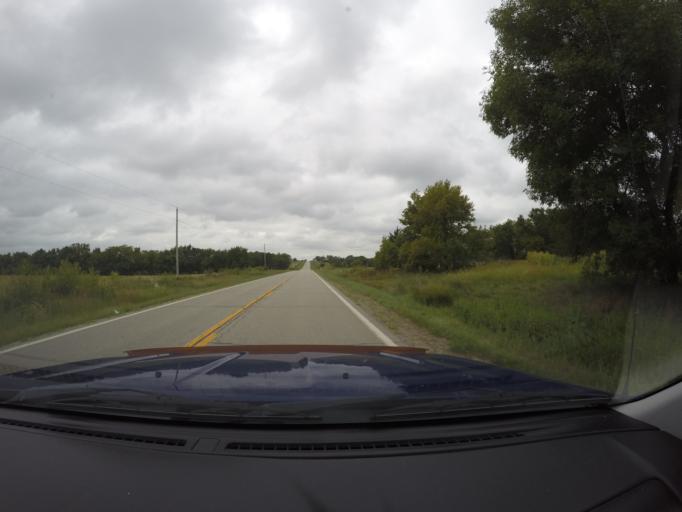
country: US
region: Kansas
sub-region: Morris County
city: Council Grove
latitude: 38.8411
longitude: -96.5702
